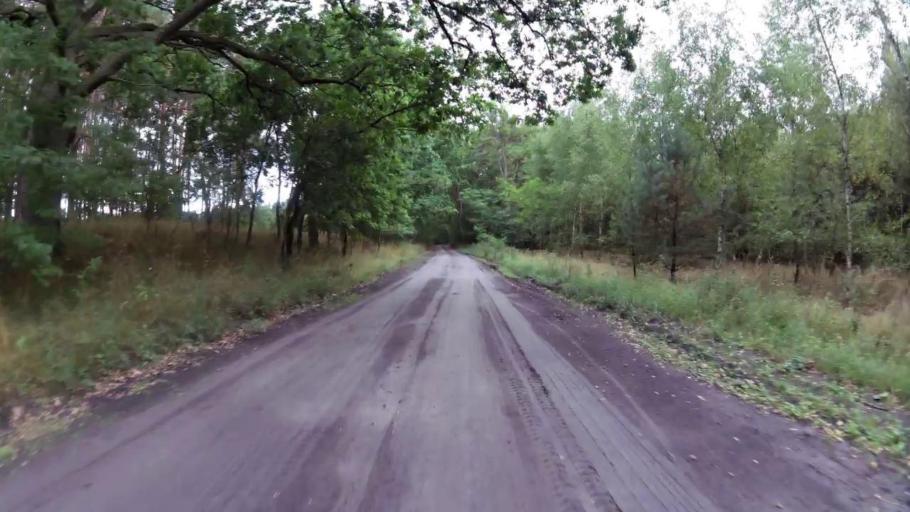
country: PL
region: West Pomeranian Voivodeship
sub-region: Powiat mysliborski
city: Debno
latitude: 52.8142
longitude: 14.7264
